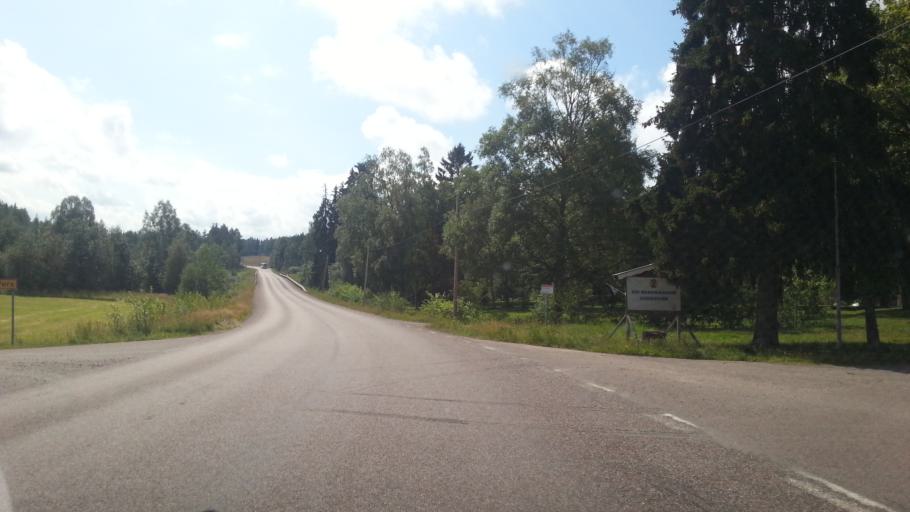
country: SE
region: Dalarna
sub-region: Faluns Kommun
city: Falun
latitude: 60.6333
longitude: 15.7686
